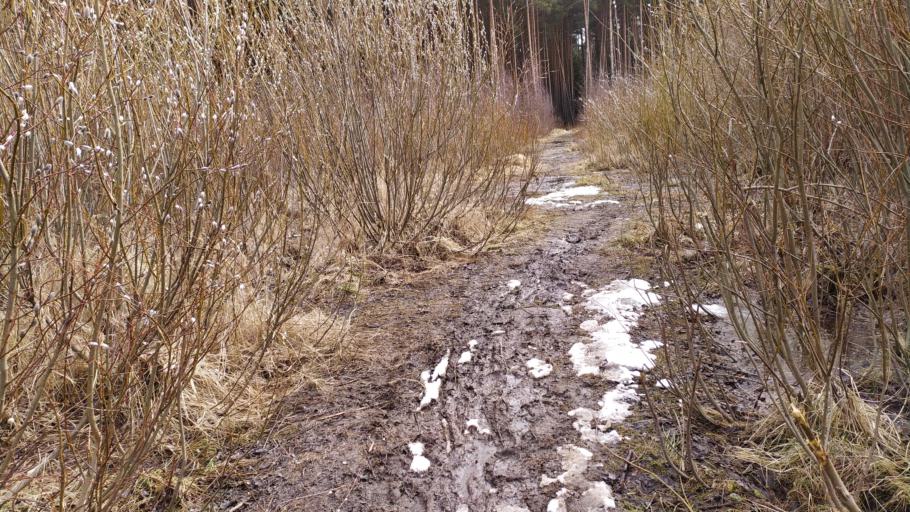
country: RU
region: St.-Petersburg
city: Krasnogvargeisky
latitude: 59.9601
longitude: 30.5020
